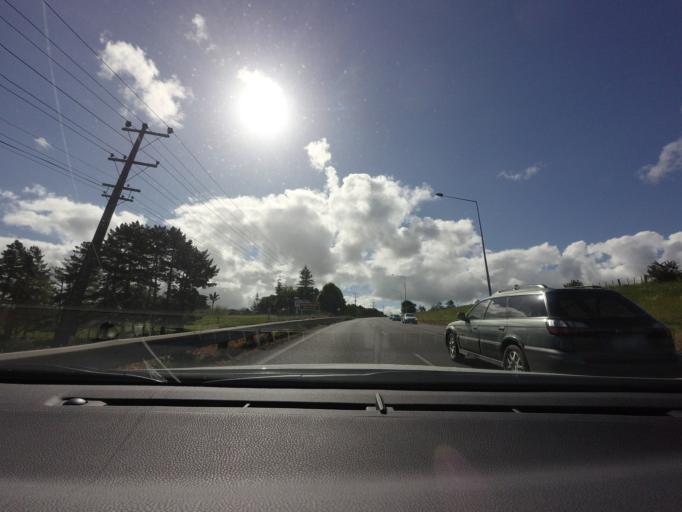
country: NZ
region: Auckland
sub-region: Auckland
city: Rosebank
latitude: -36.7921
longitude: 174.5881
